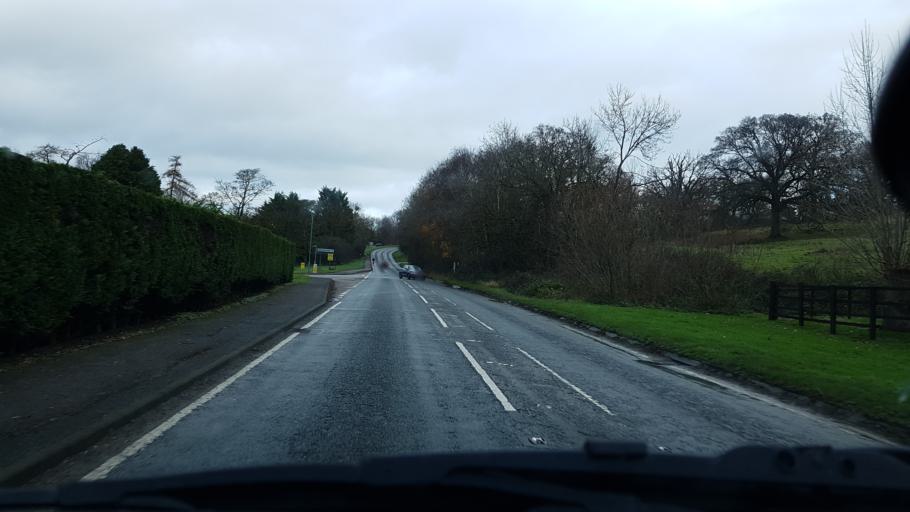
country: GB
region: England
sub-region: Gloucestershire
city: Gotherington
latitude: 51.9292
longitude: -2.0399
